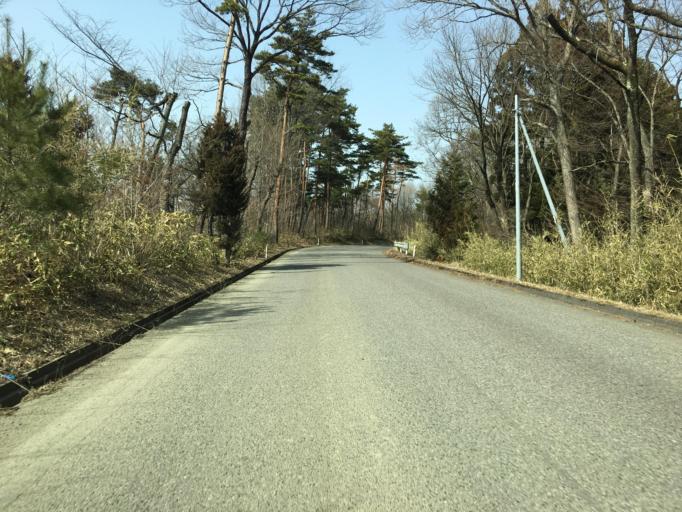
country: JP
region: Fukushima
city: Motomiya
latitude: 37.5350
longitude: 140.4107
